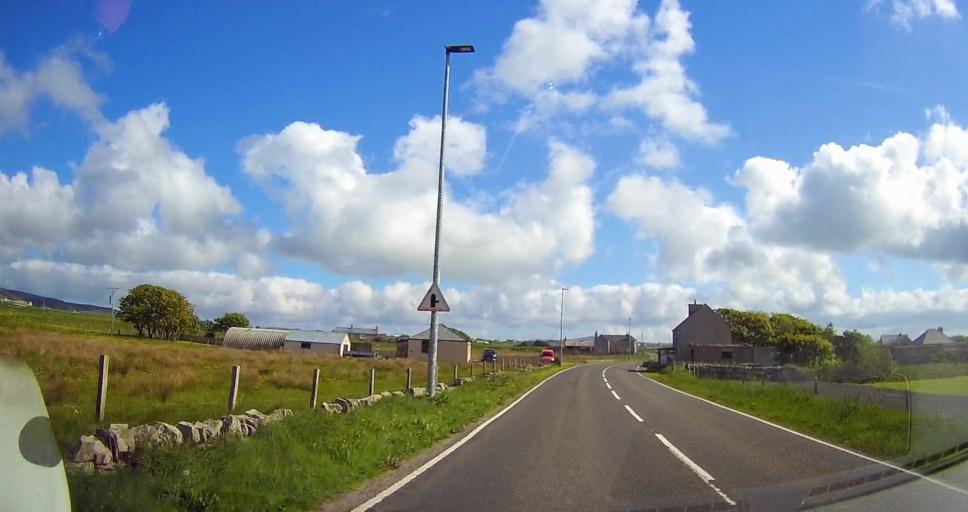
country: GB
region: Scotland
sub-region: Orkney Islands
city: Stromness
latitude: 59.0381
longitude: -3.1870
